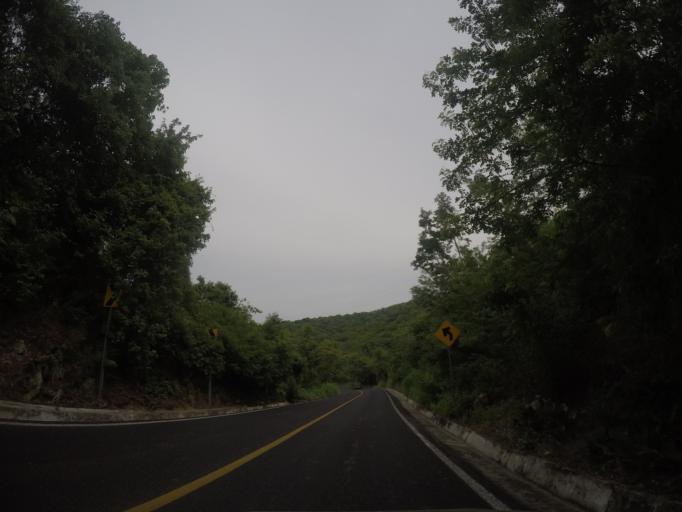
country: MX
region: Oaxaca
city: San Pedro Mixtepec
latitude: 15.9545
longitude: -97.2268
